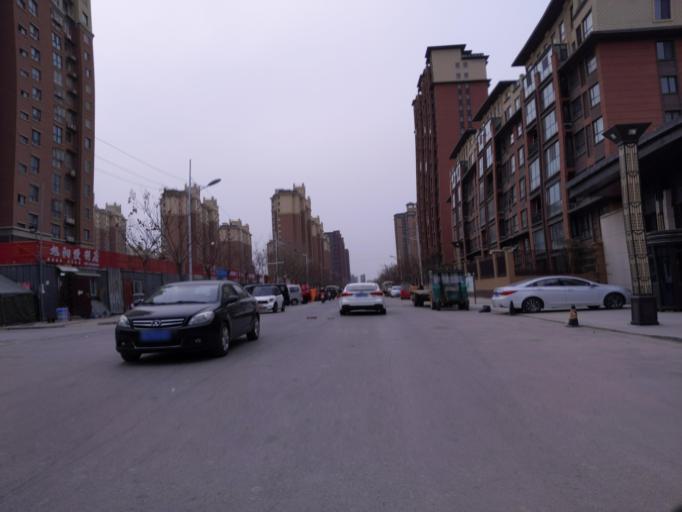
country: CN
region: Henan Sheng
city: Zhongyuanlu
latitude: 35.7423
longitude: 115.0765
